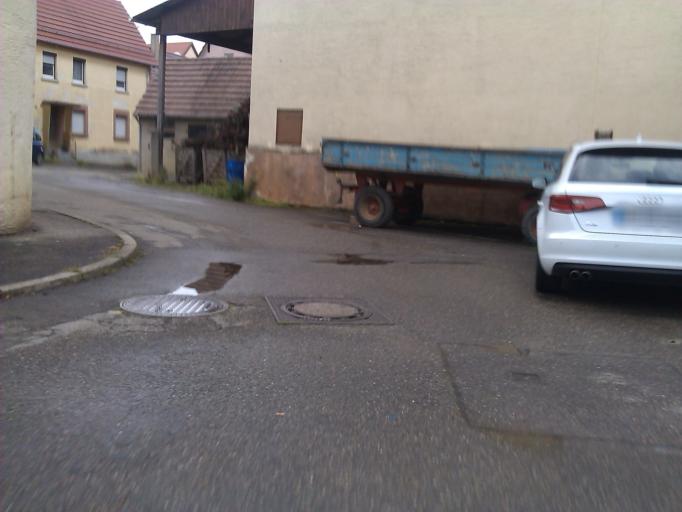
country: DE
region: Baden-Wuerttemberg
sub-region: Regierungsbezirk Stuttgart
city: Nordheim
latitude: 49.0786
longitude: 9.1052
